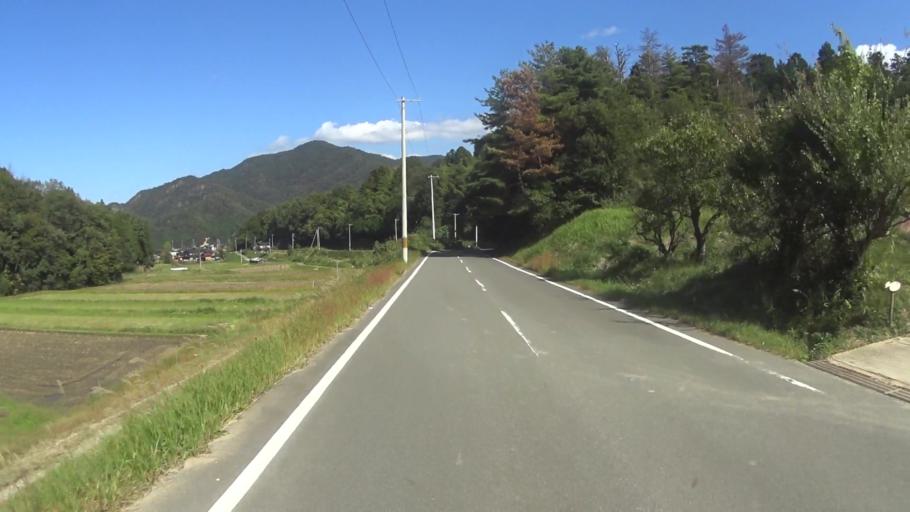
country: JP
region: Hyogo
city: Toyooka
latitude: 35.5357
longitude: 134.9358
